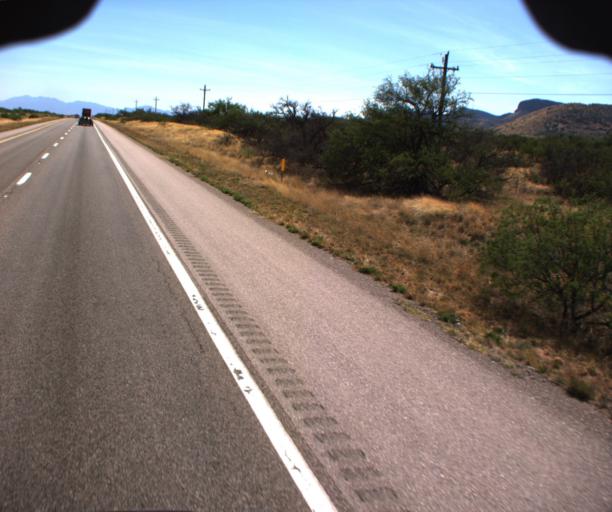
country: US
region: Arizona
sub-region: Cochise County
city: Whetstone
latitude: 31.8681
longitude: -110.3413
